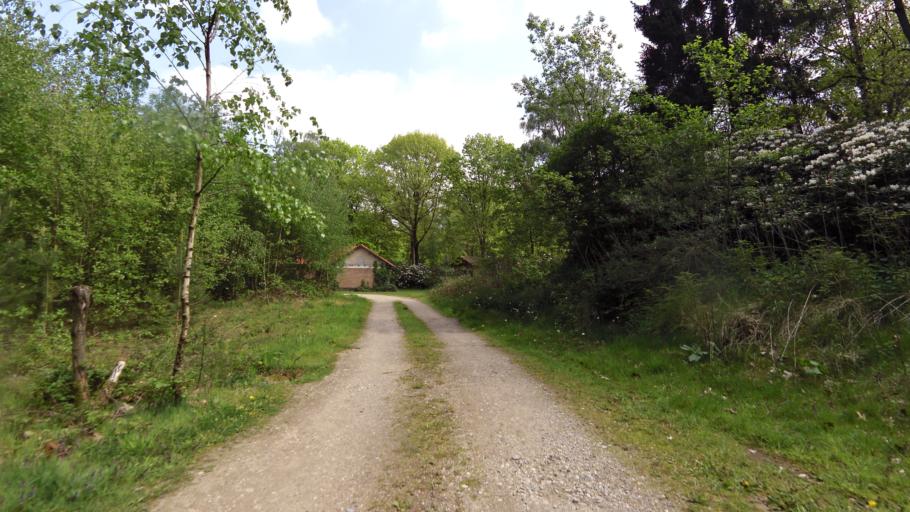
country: NL
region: Gelderland
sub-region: Gemeente Ede
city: Bennekom
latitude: 52.0199
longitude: 5.7012
